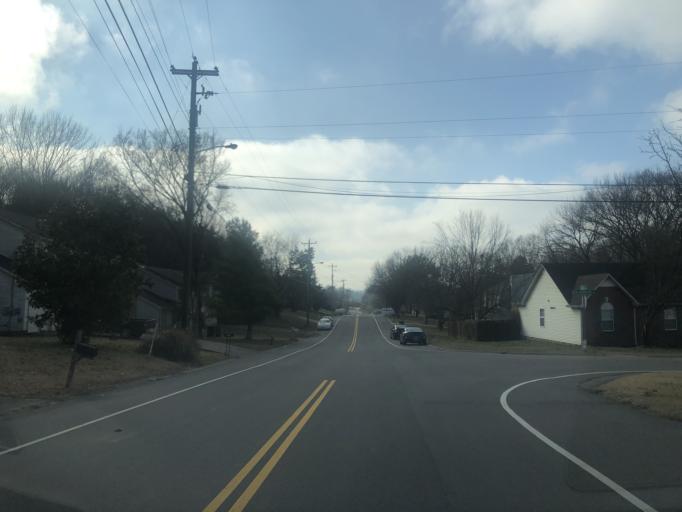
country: US
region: Tennessee
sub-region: Rutherford County
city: La Vergne
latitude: 36.0841
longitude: -86.6595
